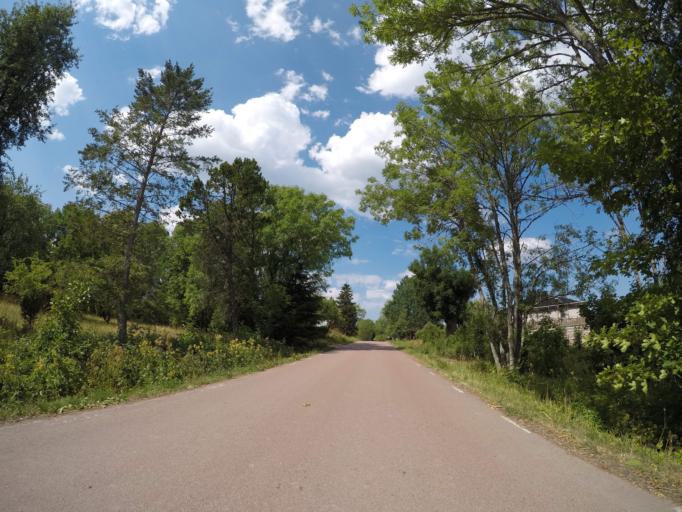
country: AX
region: Alands landsbygd
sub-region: Finstroem
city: Finstroem
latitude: 60.2504
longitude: 19.8772
